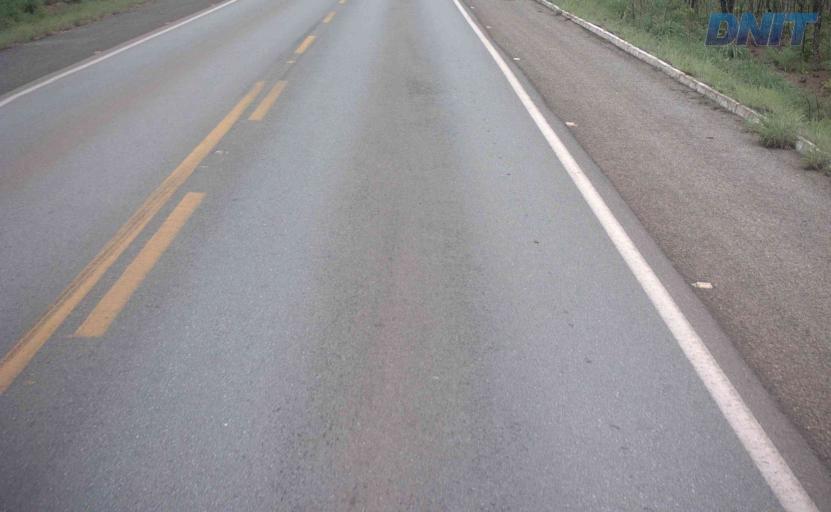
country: BR
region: Goias
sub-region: Barro Alto
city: Barro Alto
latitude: -14.7708
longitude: -49.0586
